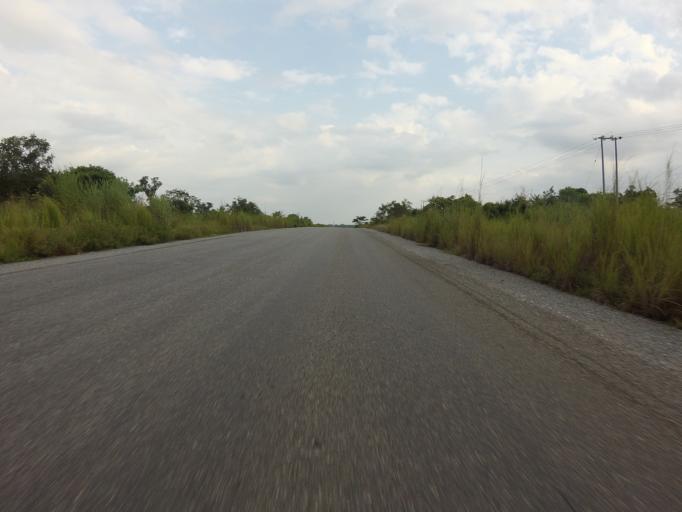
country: GH
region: Volta
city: Ho
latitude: 6.4132
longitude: 0.5215
